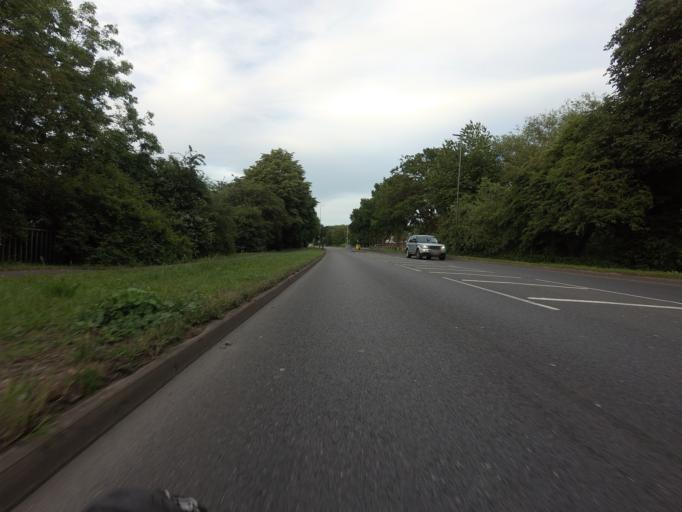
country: GB
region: England
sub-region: Greater London
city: Sidcup
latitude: 51.4137
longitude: 0.1200
